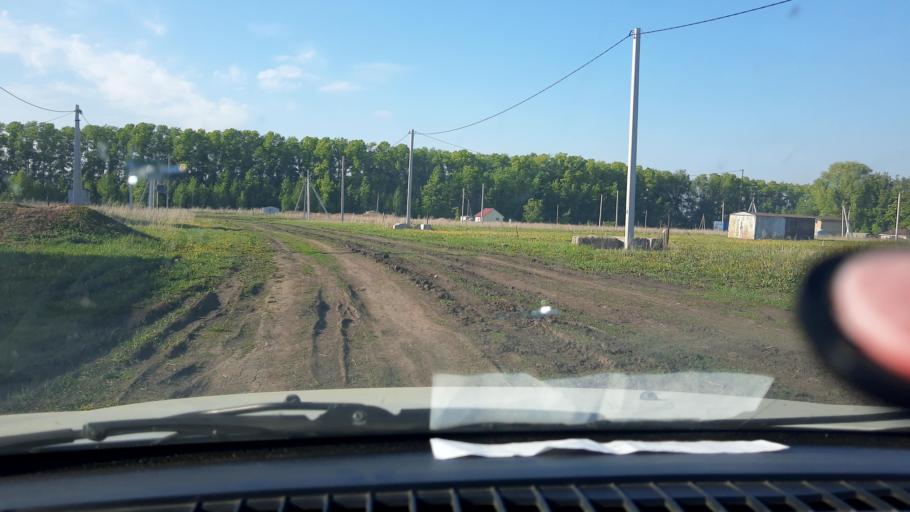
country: RU
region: Bashkortostan
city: Kabakovo
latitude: 54.6970
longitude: 56.1750
